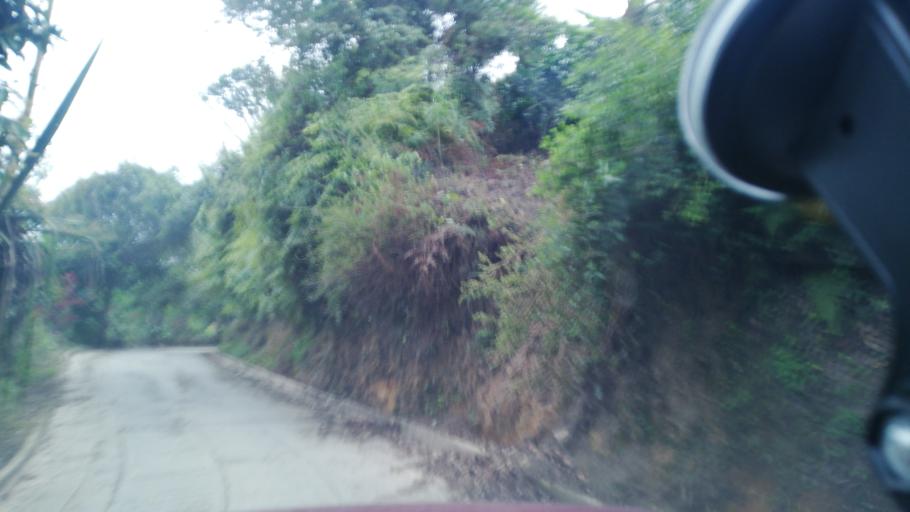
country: CO
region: Cundinamarca
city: Vergara
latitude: 5.1619
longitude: -74.2606
